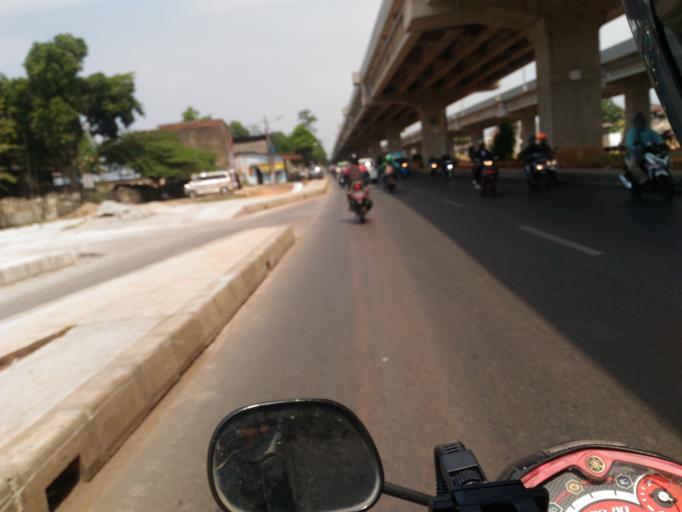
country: ID
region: Jakarta Raya
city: Jakarta
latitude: -6.2440
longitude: 106.8996
